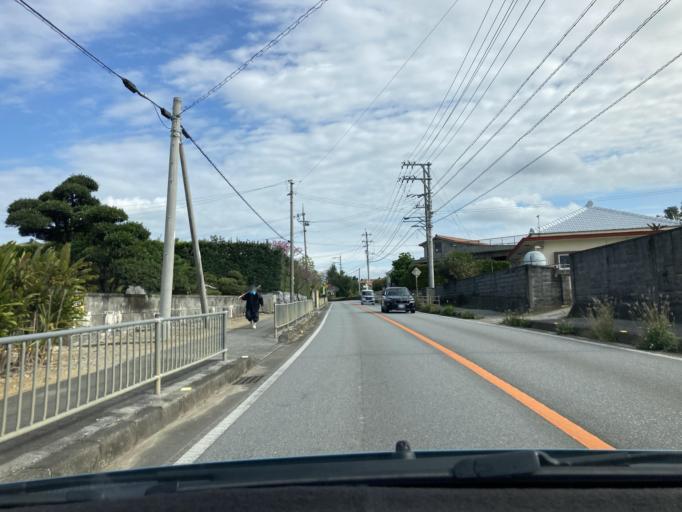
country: JP
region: Okinawa
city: Nago
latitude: 26.6975
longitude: 127.9346
